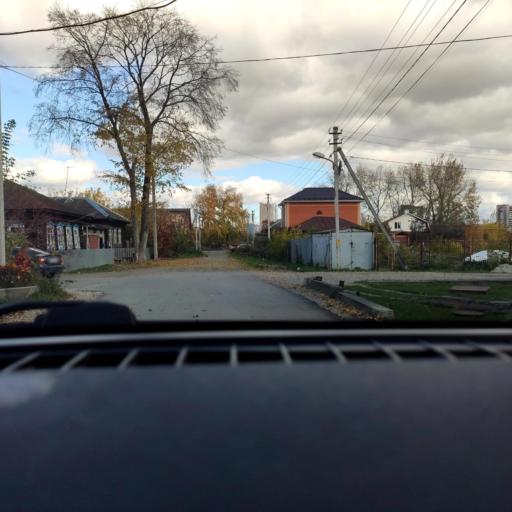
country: RU
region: Perm
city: Kondratovo
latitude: 57.9969
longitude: 56.1247
